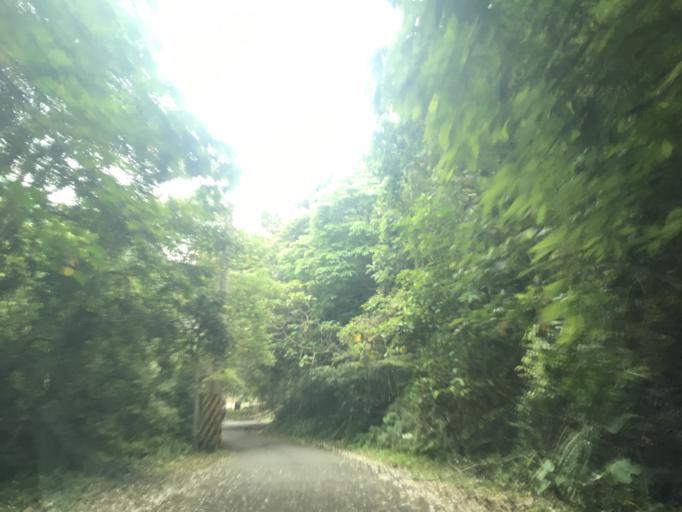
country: TW
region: Taiwan
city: Zhongxing New Village
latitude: 24.0515
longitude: 120.7796
